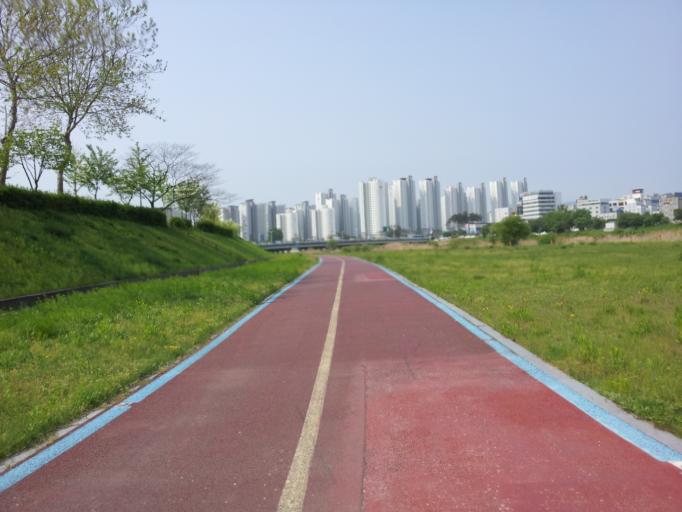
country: KR
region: Daejeon
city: Daejeon
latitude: 36.3541
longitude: 127.3532
